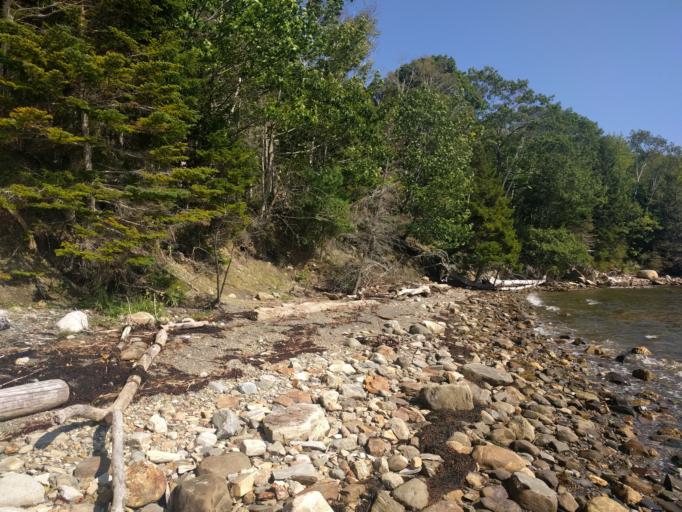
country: US
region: Maine
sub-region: Waldo County
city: Belfast
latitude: 44.4295
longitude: -68.9469
